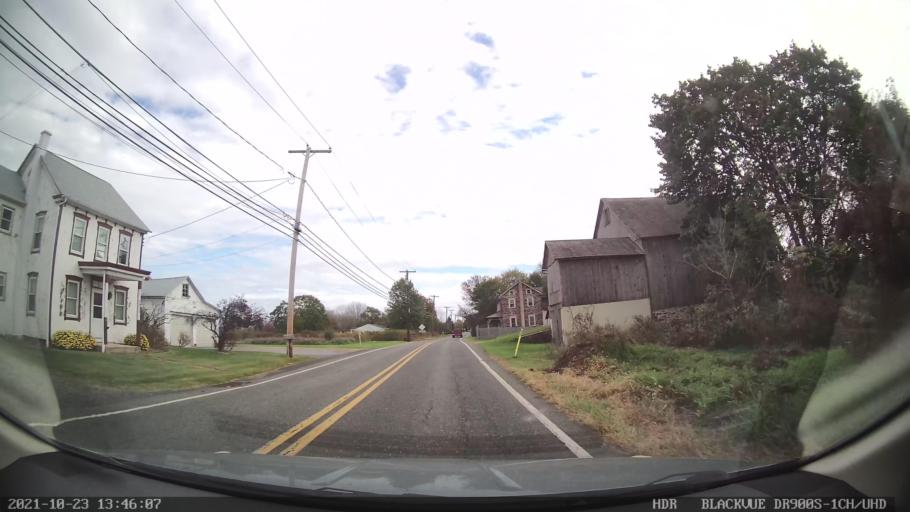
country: US
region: Pennsylvania
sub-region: Montgomery County
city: Pennsburg
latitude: 40.3771
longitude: -75.5192
